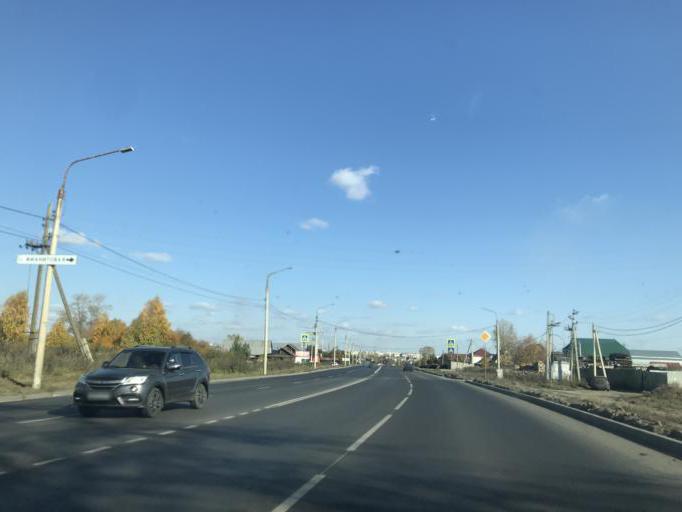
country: RU
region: Chelyabinsk
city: Dolgoderevenskoye
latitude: 55.2399
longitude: 61.3434
